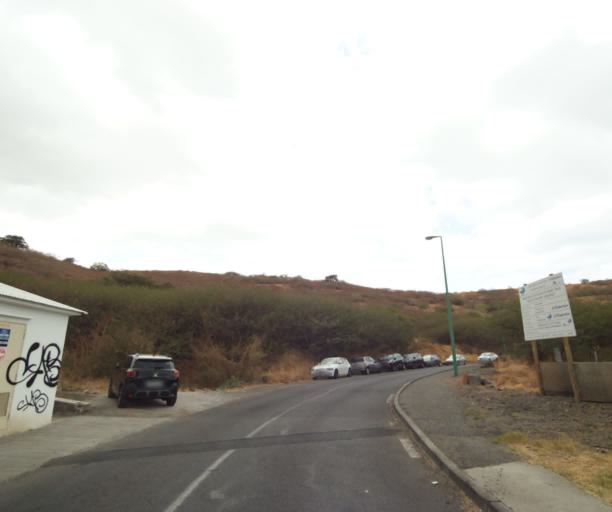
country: RE
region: Reunion
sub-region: Reunion
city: Saint-Paul
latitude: -21.0587
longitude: 55.2331
